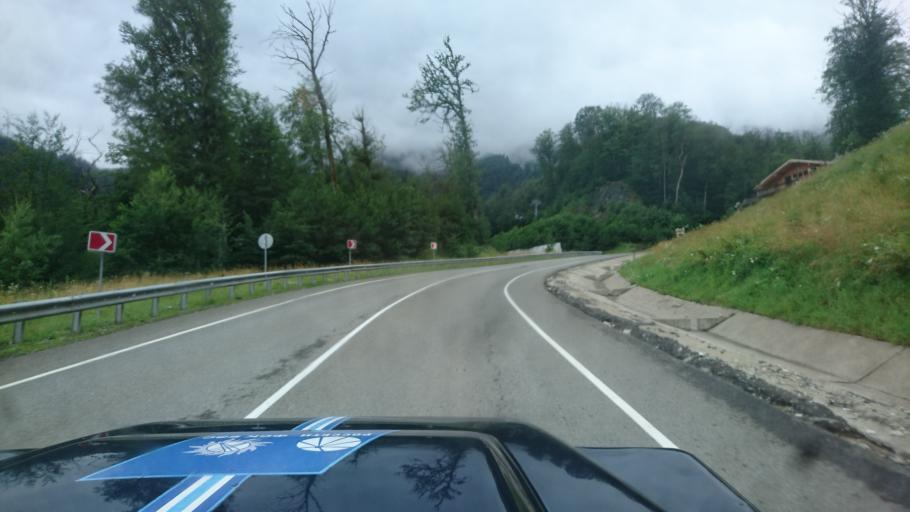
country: RU
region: Krasnodarskiy
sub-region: Sochi City
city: Krasnaya Polyana
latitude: 43.6673
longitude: 40.3004
